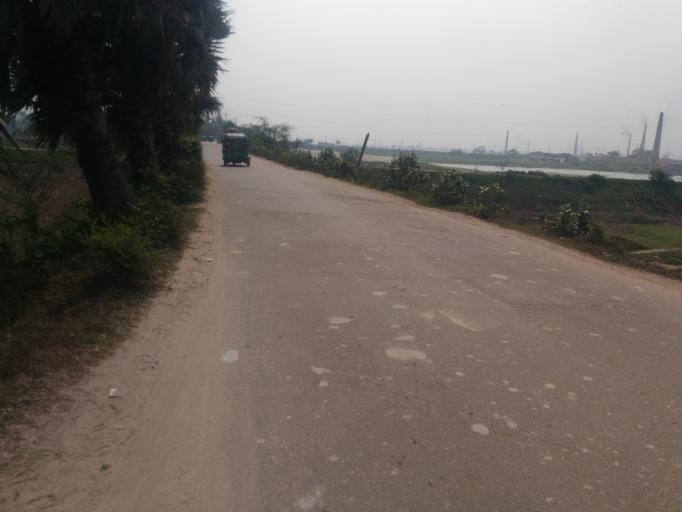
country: BD
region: Dhaka
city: Narayanganj
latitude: 23.6404
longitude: 90.4508
